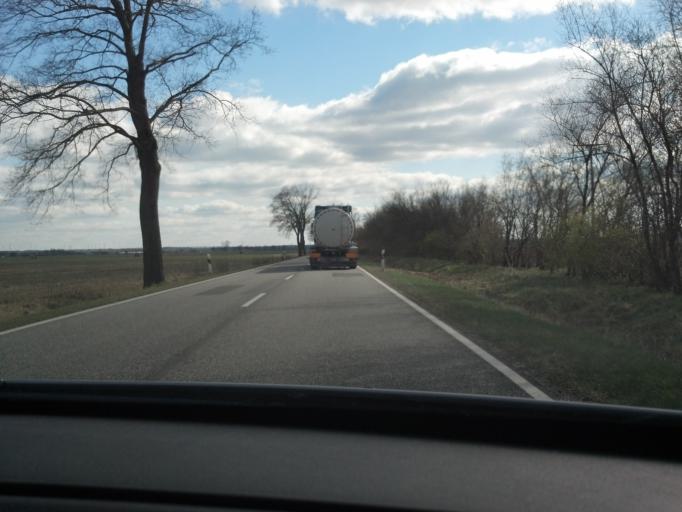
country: DE
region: Mecklenburg-Vorpommern
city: Plau am See
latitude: 53.3614
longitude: 12.2471
